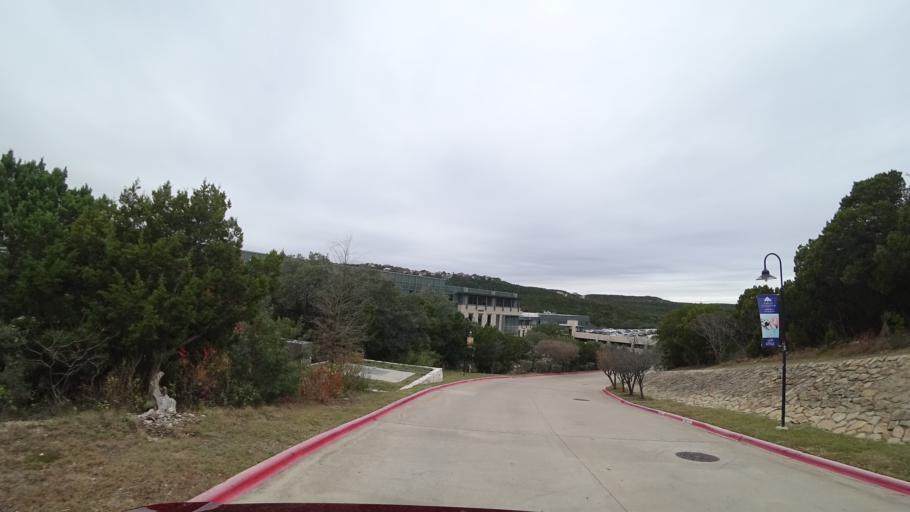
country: US
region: Texas
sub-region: Travis County
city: West Lake Hills
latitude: 30.3630
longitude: -97.7921
